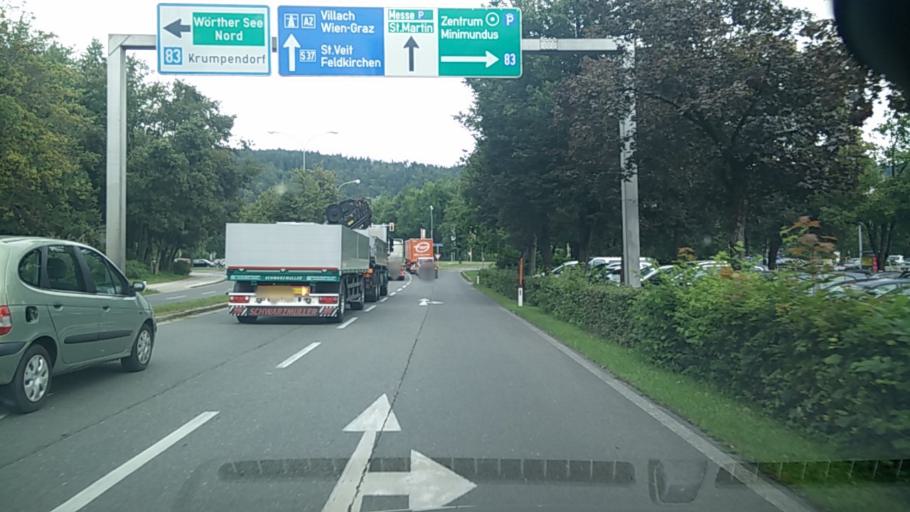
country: AT
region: Carinthia
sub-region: Klagenfurt am Woerthersee
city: Klagenfurt am Woerthersee
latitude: 46.6200
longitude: 14.2626
